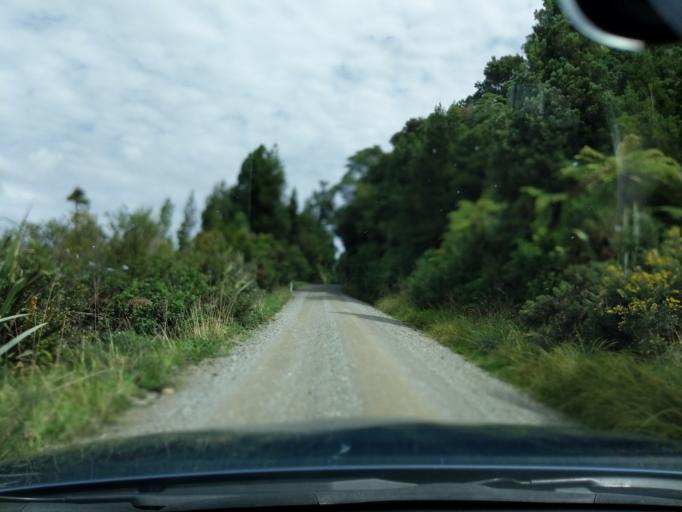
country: NZ
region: Tasman
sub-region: Tasman District
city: Takaka
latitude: -40.6433
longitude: 172.4806
